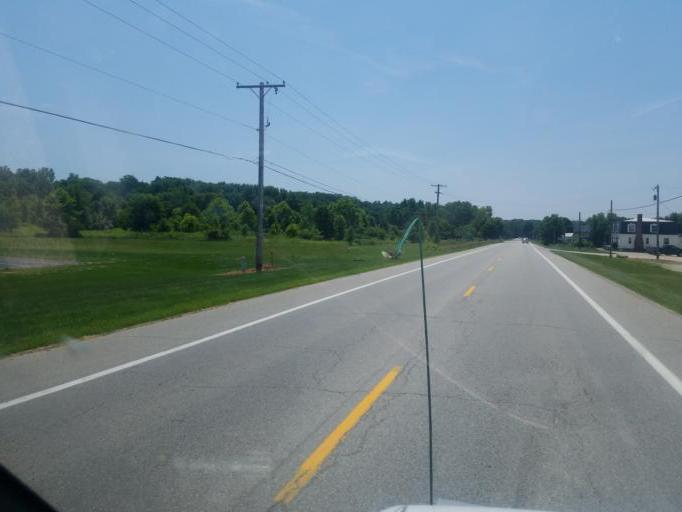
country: US
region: Ohio
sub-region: Shelby County
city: Sidney
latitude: 40.3004
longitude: -84.1397
